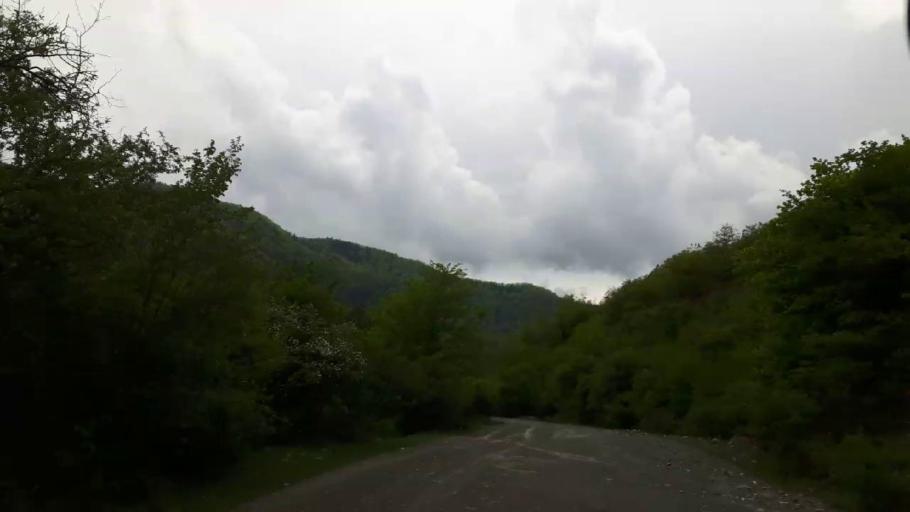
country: GE
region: Shida Kartli
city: Gori
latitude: 41.8709
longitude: 43.9855
